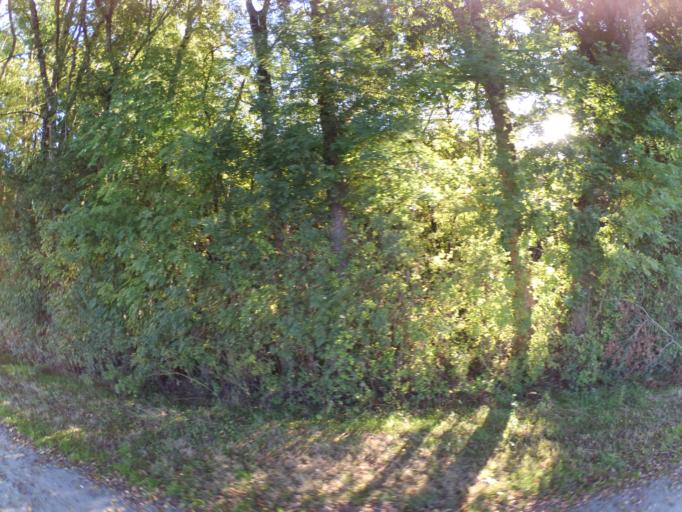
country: FR
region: Brittany
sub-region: Departement du Morbihan
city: Peillac
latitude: 47.7243
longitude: -2.2011
